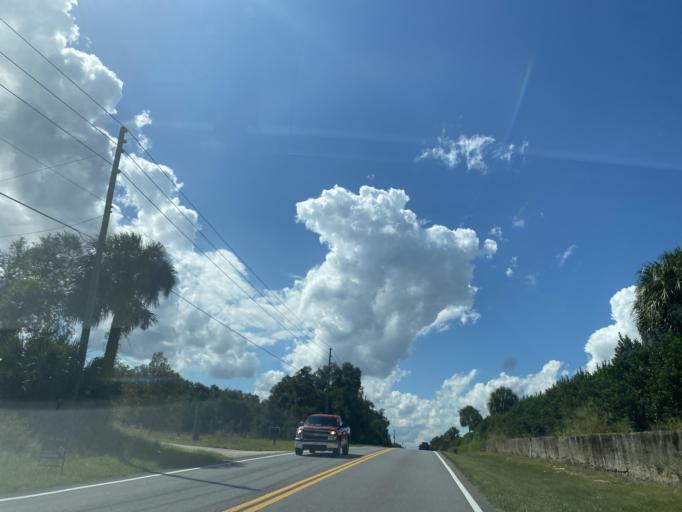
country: US
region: Florida
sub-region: Lake County
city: Lady Lake
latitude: 28.9819
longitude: -81.9135
